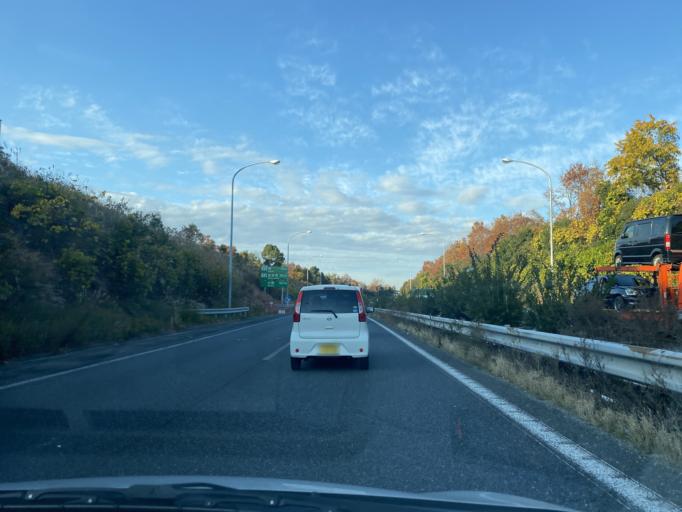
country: JP
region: Osaka
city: Izumi
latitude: 34.4501
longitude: 135.4453
